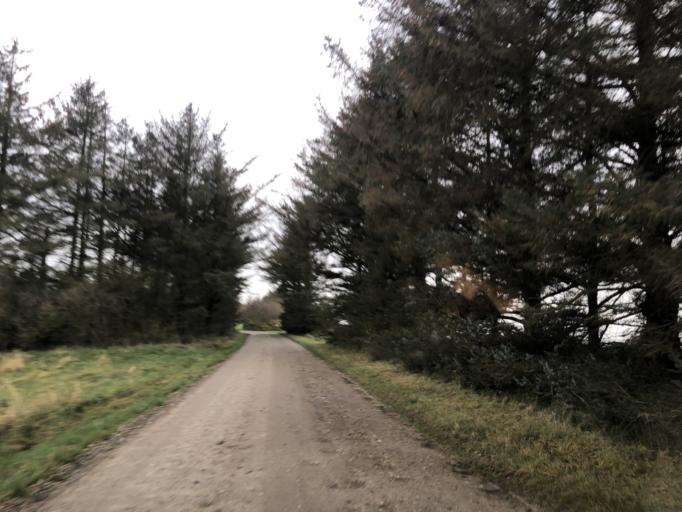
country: DK
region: Central Jutland
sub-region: Holstebro Kommune
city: Ulfborg
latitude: 56.3202
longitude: 8.2264
